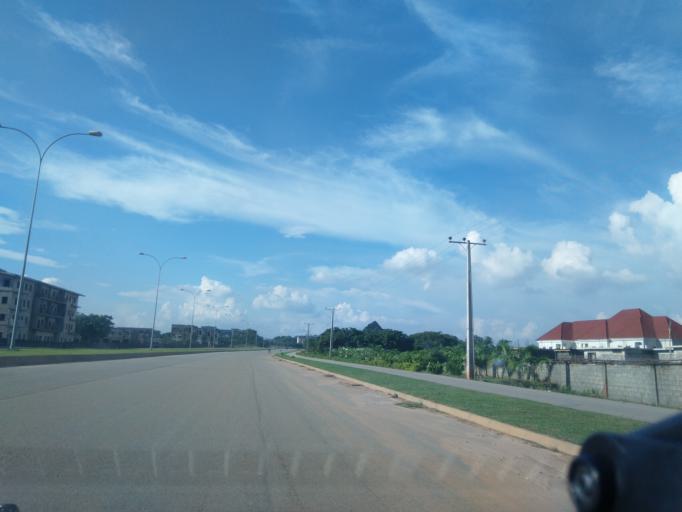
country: NG
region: Abuja Federal Capital Territory
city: Abuja
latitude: 9.0522
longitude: 7.3900
